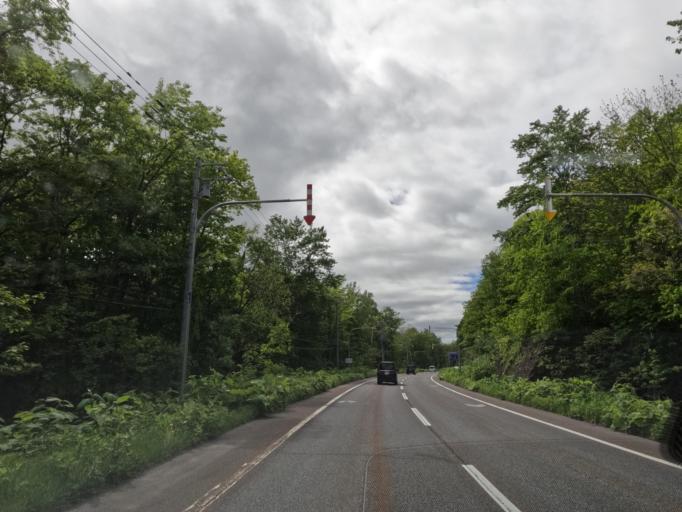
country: JP
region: Hokkaido
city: Kamikawa
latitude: 43.8175
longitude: 142.8490
